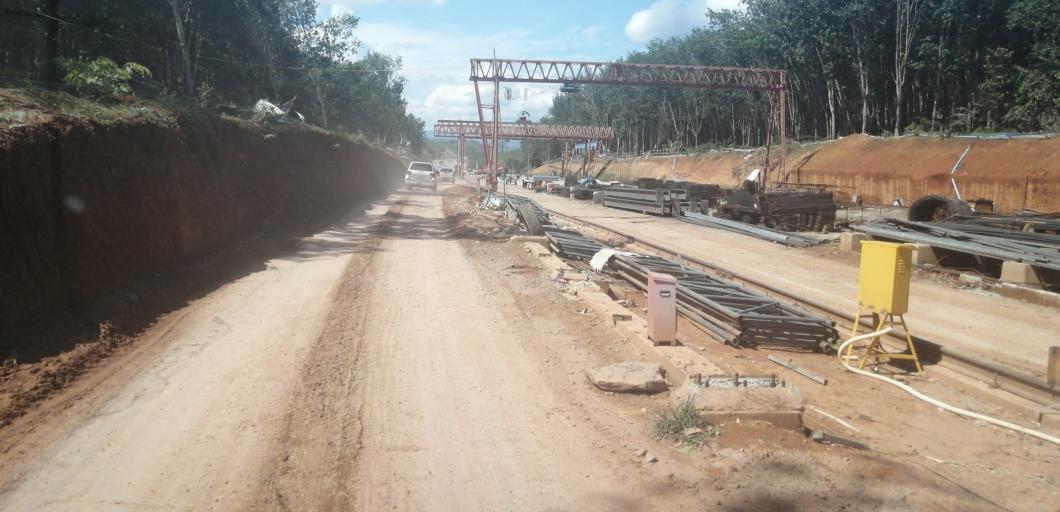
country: LA
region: Vientiane
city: Vangviang
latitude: 18.7472
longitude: 102.3838
